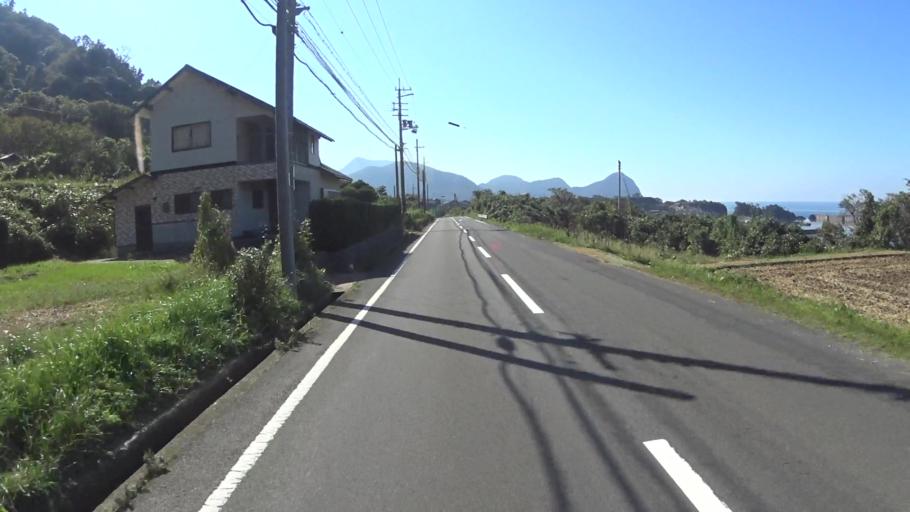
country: JP
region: Kyoto
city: Miyazu
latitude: 35.7617
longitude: 135.1847
